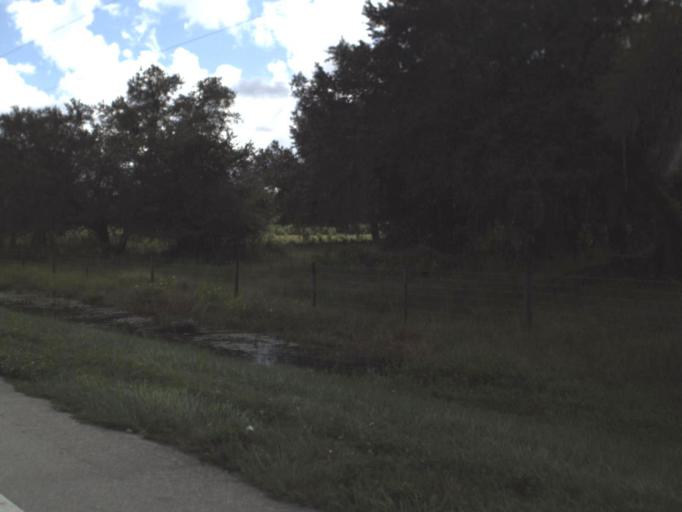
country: US
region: Florida
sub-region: DeSoto County
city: Arcadia
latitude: 27.2722
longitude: -82.0084
